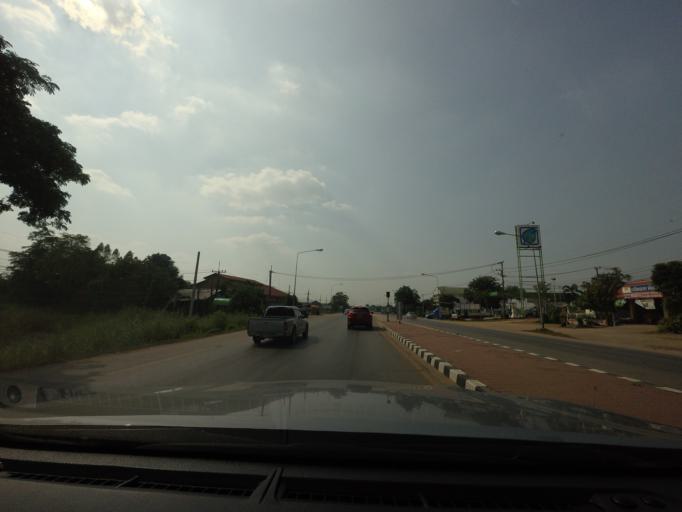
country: TH
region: Phitsanulok
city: Bang Rakam
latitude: 16.7461
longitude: 100.1103
